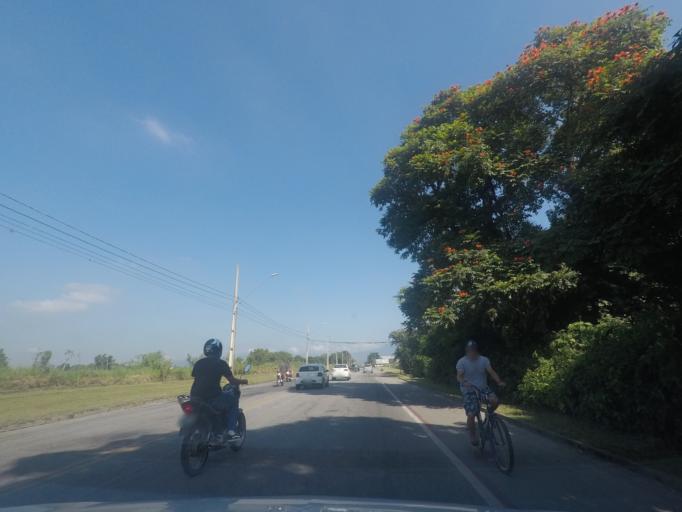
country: BR
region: Parana
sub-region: Paranagua
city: Paranagua
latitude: -25.5396
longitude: -48.5335
